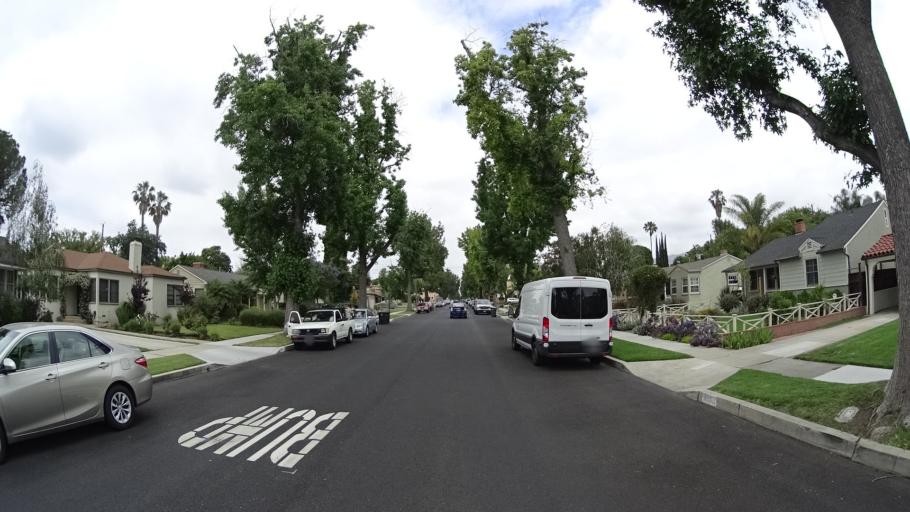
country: US
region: California
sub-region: Los Angeles County
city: Burbank
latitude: 34.1733
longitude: -118.3248
